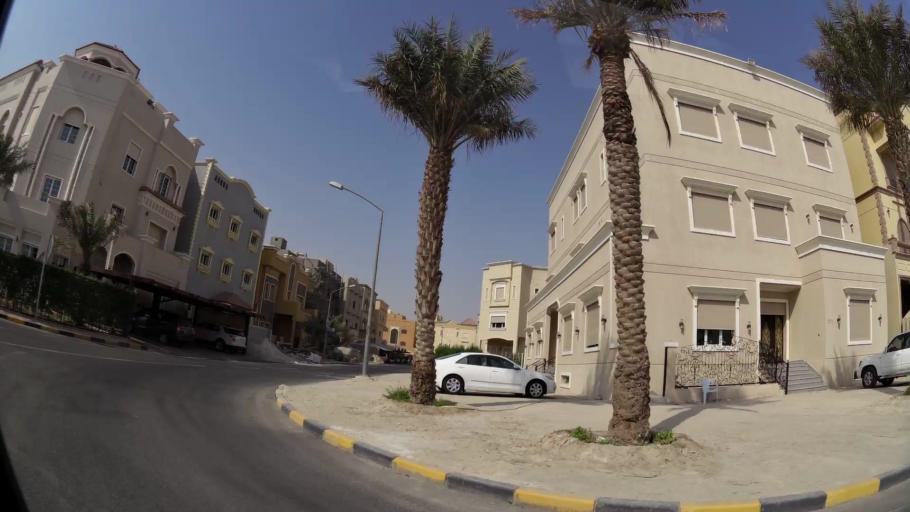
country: KW
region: Muhafazat al Jahra'
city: Al Jahra'
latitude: 29.3301
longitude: 47.7806
